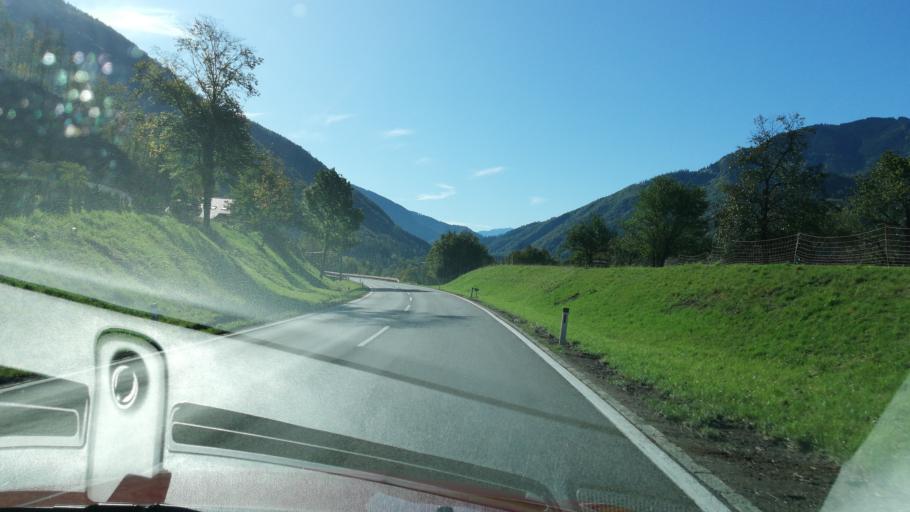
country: AT
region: Upper Austria
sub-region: Politischer Bezirk Steyr-Land
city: Weyer
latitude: 47.8127
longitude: 14.6427
